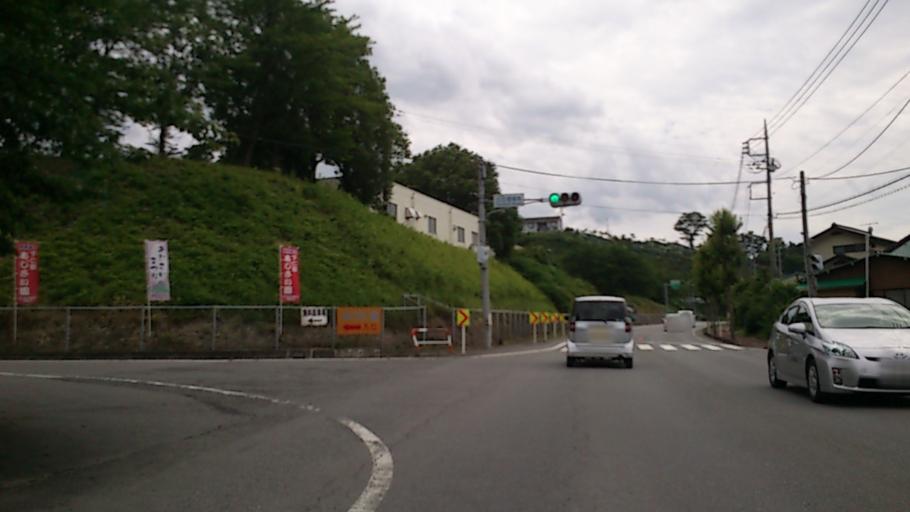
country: JP
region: Gunma
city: Tomioka
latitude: 36.2345
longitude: 138.8224
